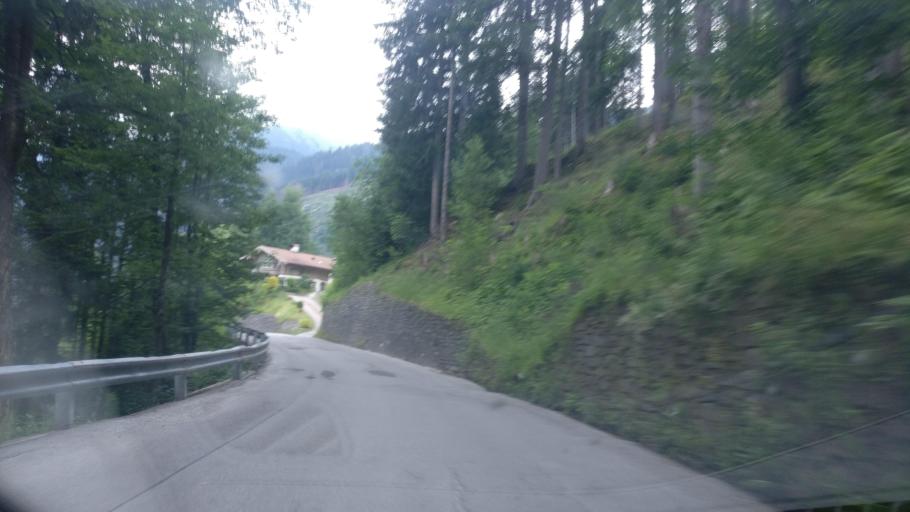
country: AT
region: Salzburg
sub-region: Politischer Bezirk Sankt Johann im Pongau
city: Bad Gastein
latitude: 47.1223
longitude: 13.1457
